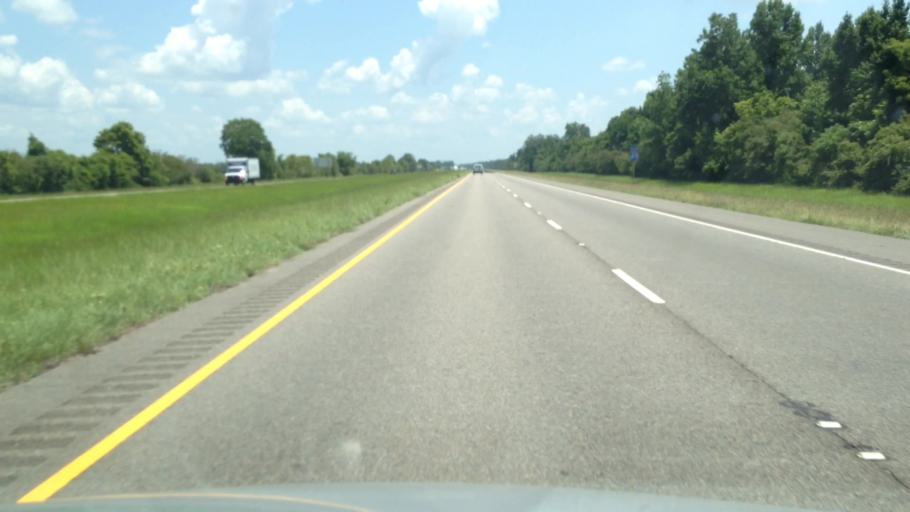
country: US
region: Louisiana
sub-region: Avoyelles Parish
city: Bunkie
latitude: 30.9458
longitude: -92.2711
